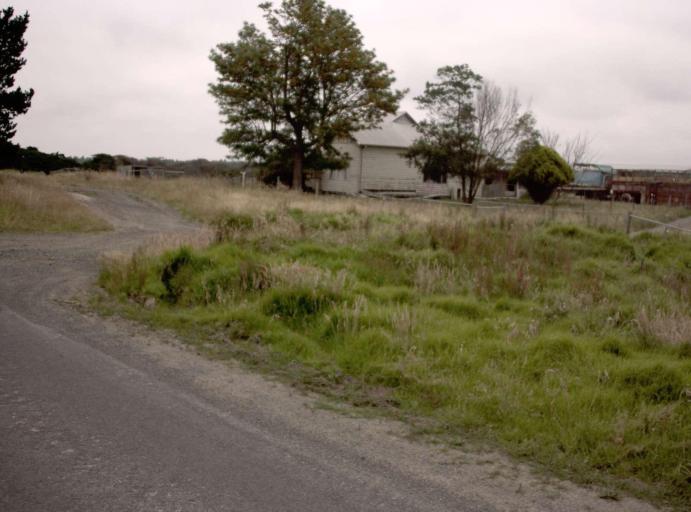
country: AU
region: Victoria
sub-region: Latrobe
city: Morwell
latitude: -38.2829
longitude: 146.3714
